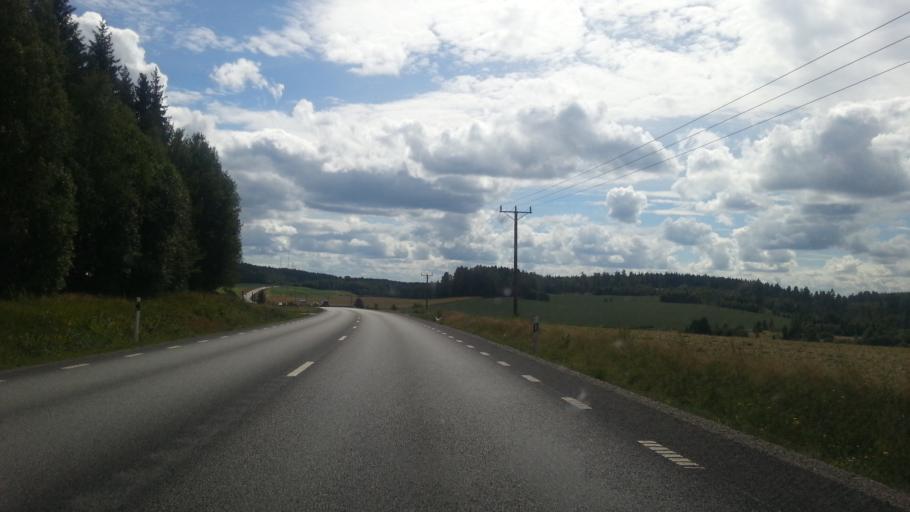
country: SE
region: OErebro
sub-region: Lindesbergs Kommun
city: Lindesberg
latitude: 59.5909
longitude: 15.1866
